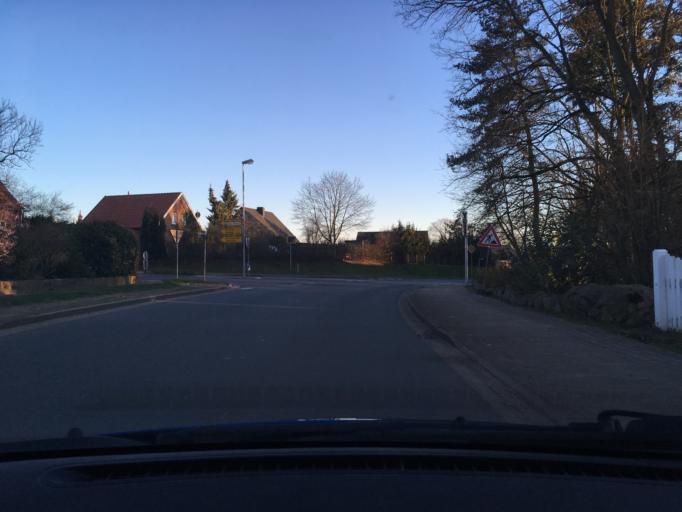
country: DE
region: Lower Saxony
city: Dahlem
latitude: 53.1874
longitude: 10.7532
